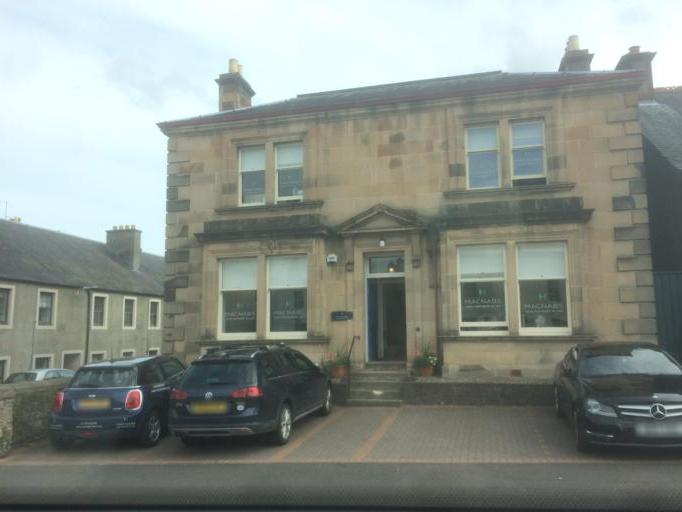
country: GB
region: Scotland
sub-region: Perth and Kinross
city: Perth
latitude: 56.4009
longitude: -3.4341
